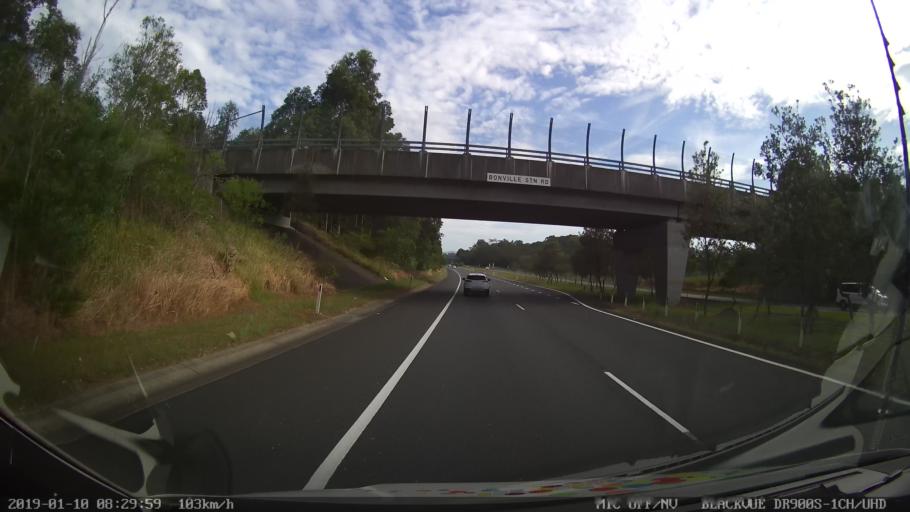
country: AU
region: New South Wales
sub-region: Coffs Harbour
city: Bonville
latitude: -30.3764
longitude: 153.0514
